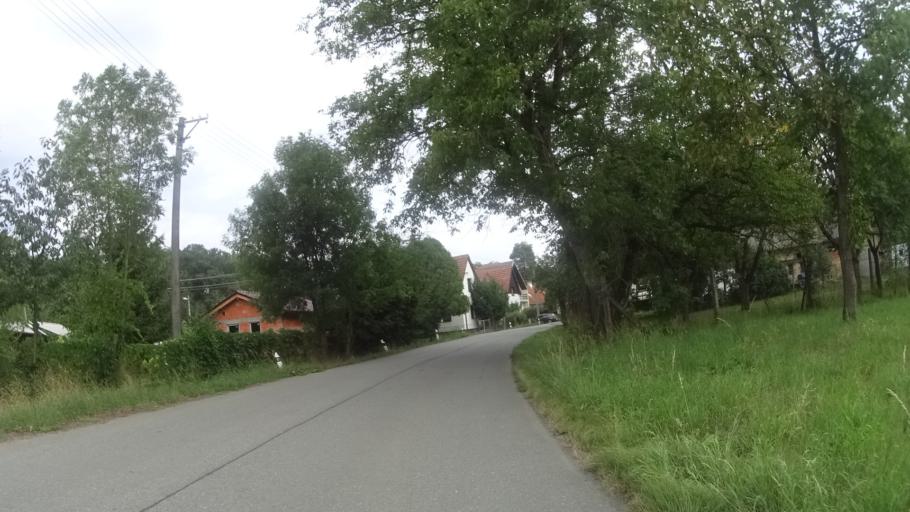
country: CZ
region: Zlin
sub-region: Okres Kromeriz
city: Kromeriz
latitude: 49.3236
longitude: 17.3879
